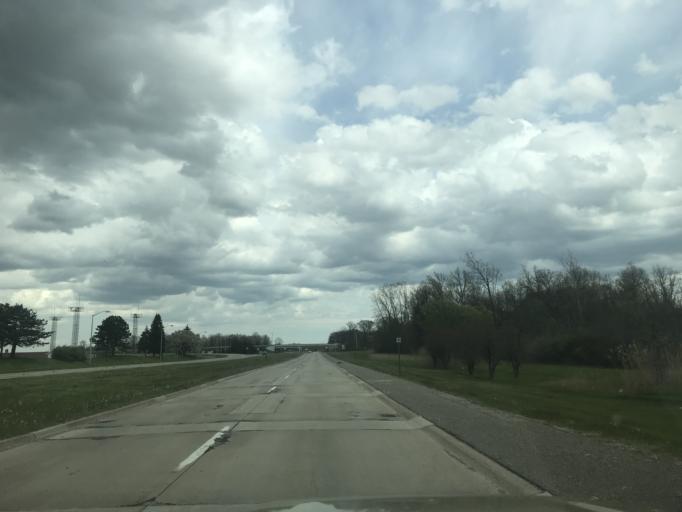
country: US
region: Michigan
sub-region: Wayne County
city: Romulus
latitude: 42.1937
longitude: -83.3715
